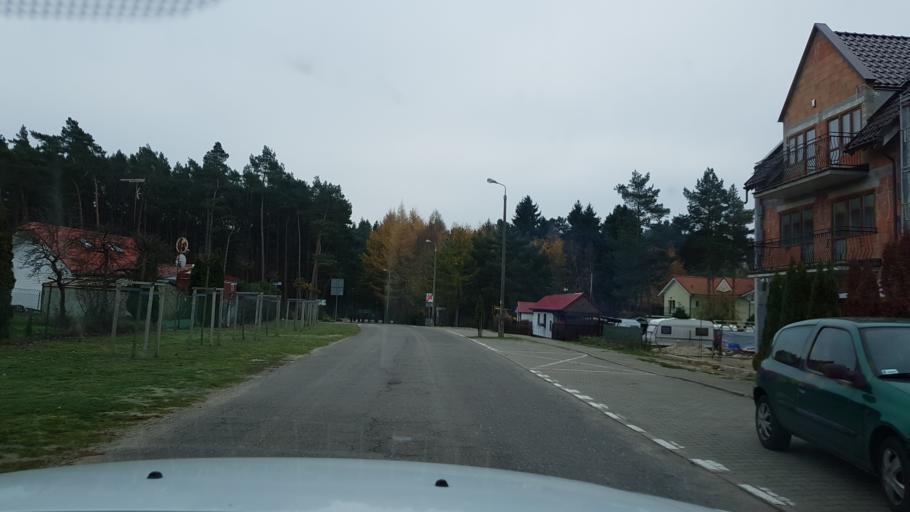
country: PL
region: West Pomeranian Voivodeship
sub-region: Powiat gryficki
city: Pobierowo
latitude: 54.0676
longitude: 14.9689
